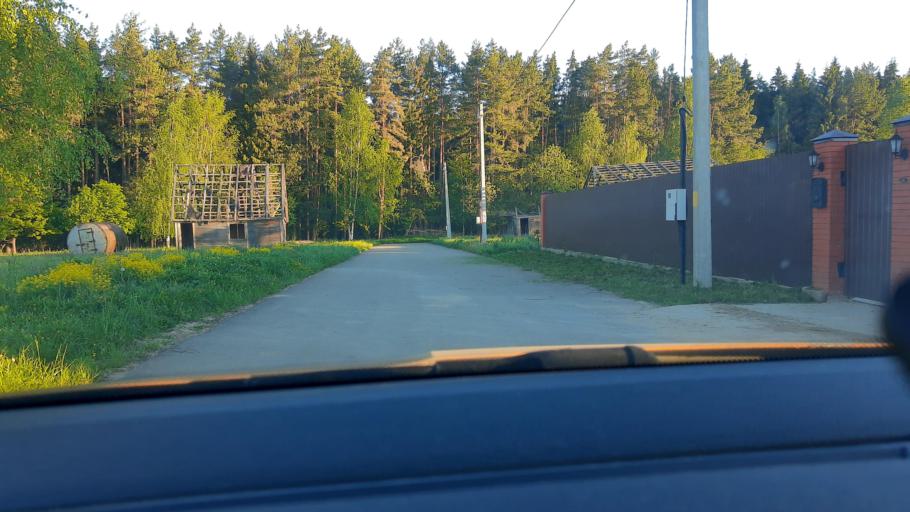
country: RU
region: Moskovskaya
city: Selyatino
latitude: 55.5065
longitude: 36.9246
